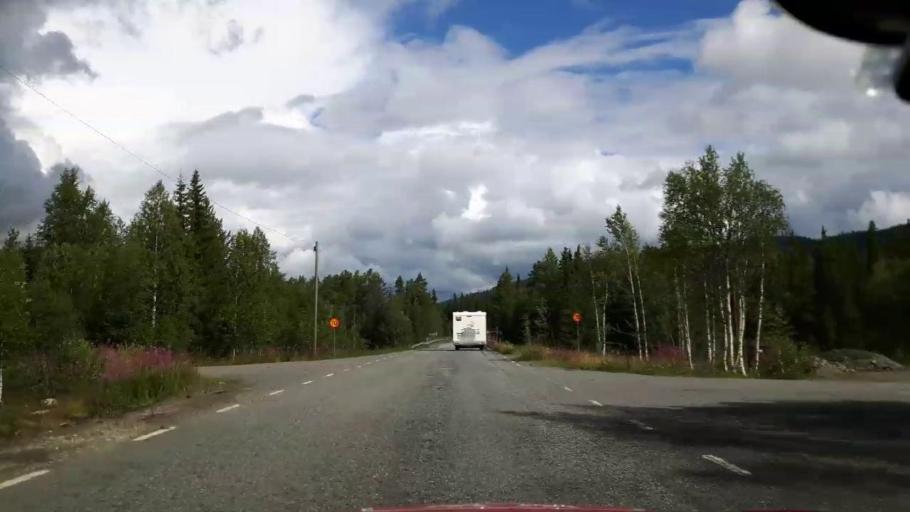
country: SE
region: Vaesterbotten
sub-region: Vilhelmina Kommun
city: Sjoberg
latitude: 64.9356
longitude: 15.8578
